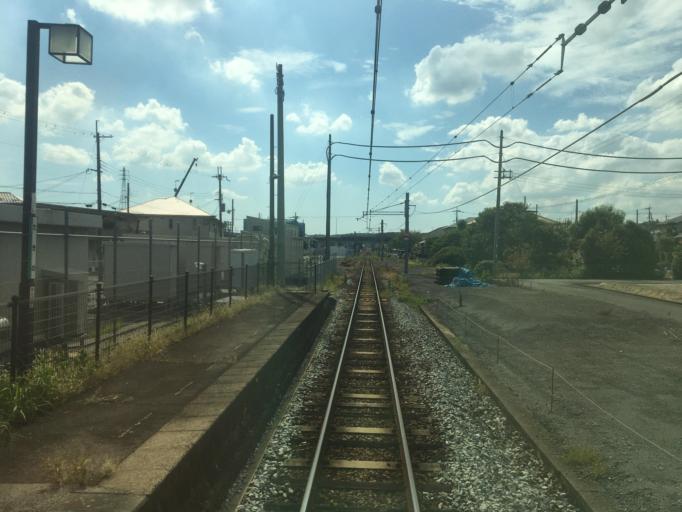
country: JP
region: Hyogo
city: Yashiro
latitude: 34.9411
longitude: 134.9551
